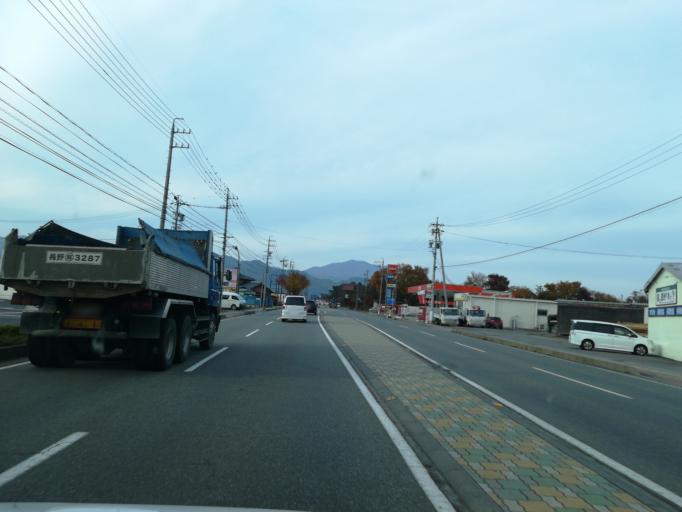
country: JP
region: Nagano
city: Nagano-shi
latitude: 36.5870
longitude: 138.1878
